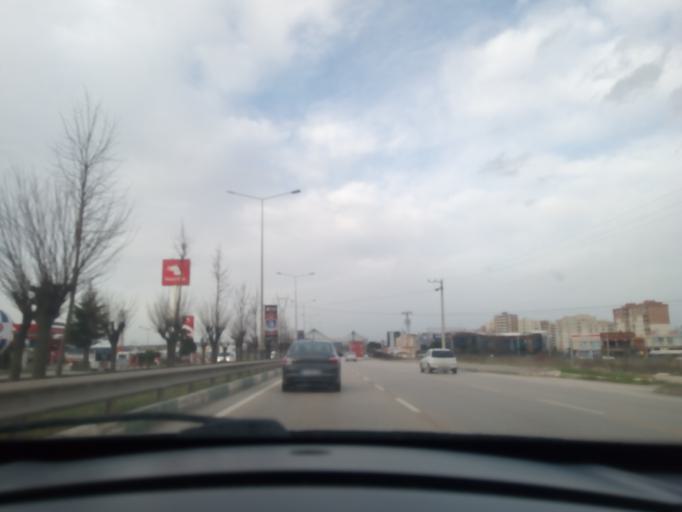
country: TR
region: Bursa
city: Cali
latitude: 40.2148
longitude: 28.9009
